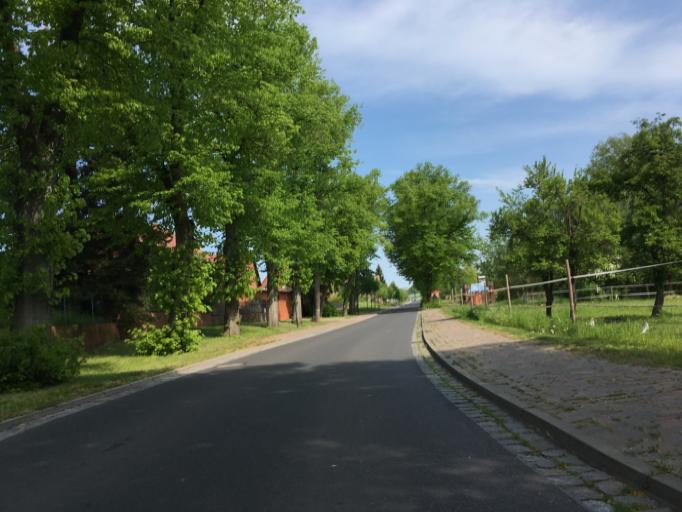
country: DE
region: Brandenburg
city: Werneuchen
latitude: 52.6033
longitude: 13.7560
